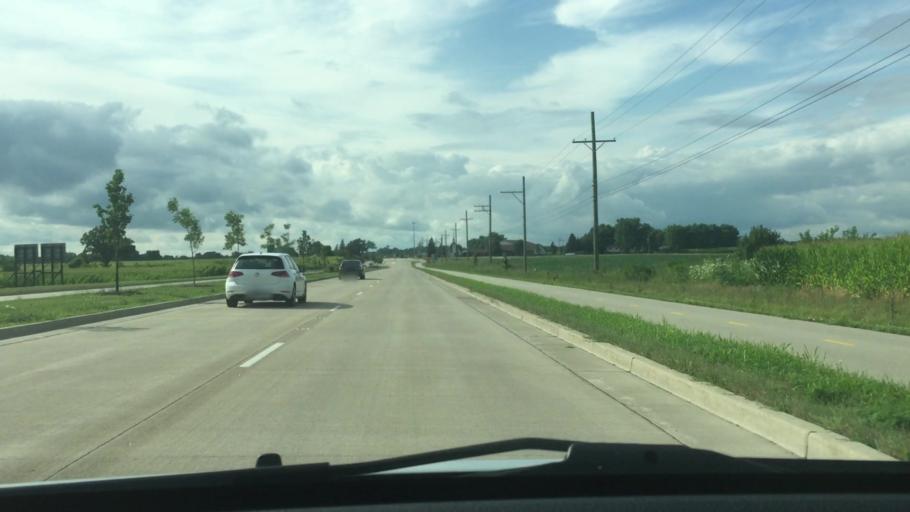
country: US
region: Illinois
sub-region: McHenry County
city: Lakewood
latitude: 42.2635
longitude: -88.3751
